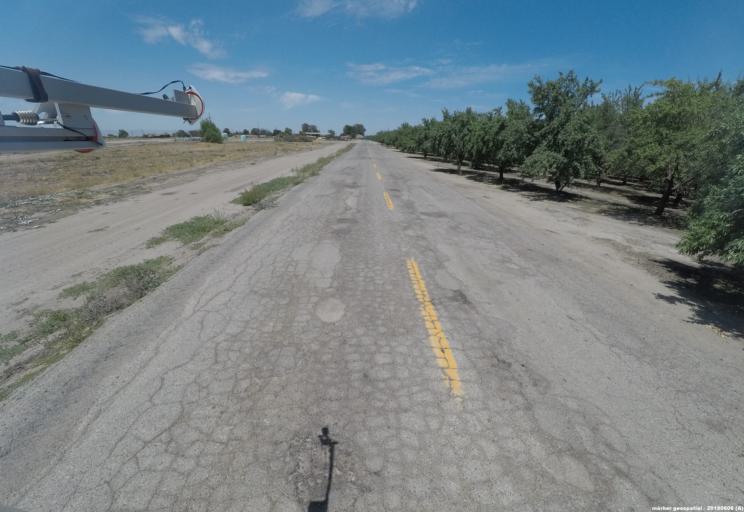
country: US
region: California
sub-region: Fresno County
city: Firebaugh
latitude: 36.8585
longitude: -120.4040
